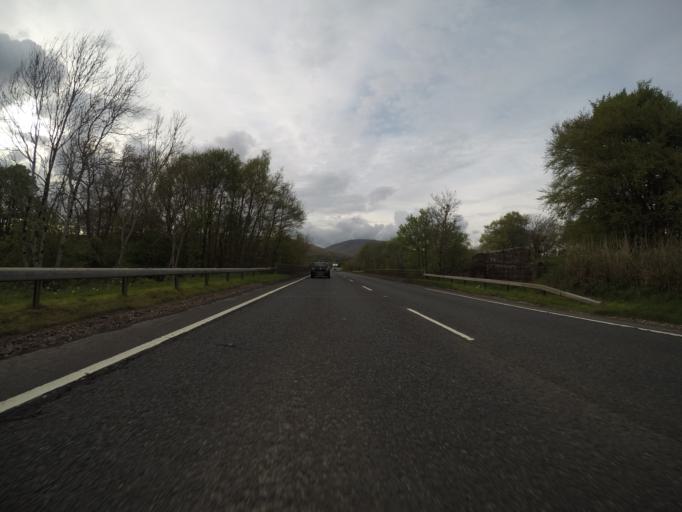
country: GB
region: Scotland
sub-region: West Dunbartonshire
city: Balloch
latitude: 56.0352
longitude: -4.6399
